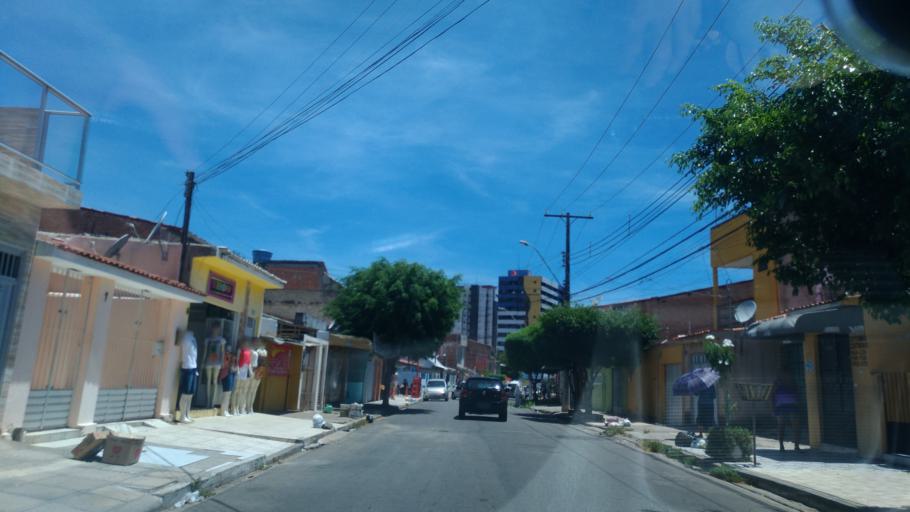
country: BR
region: Alagoas
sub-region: Maceio
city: Maceio
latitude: -9.6632
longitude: -35.7118
